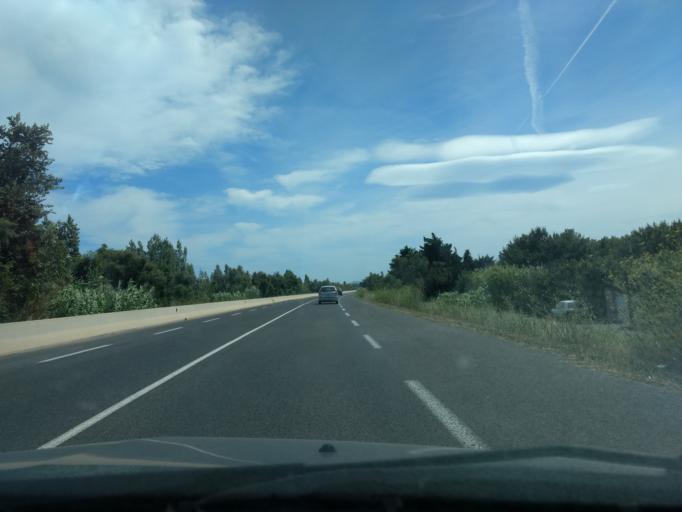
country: FR
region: Languedoc-Roussillon
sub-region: Departement des Pyrenees-Orientales
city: Sainte-Marie-Plage
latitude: 42.7274
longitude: 3.0289
